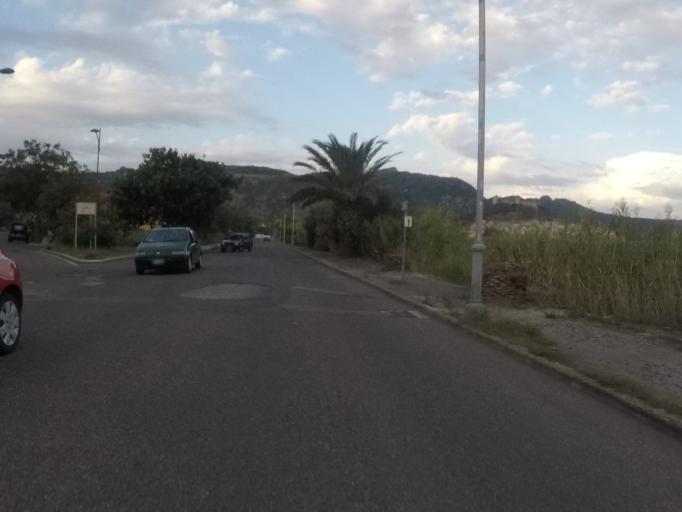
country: IT
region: Sardinia
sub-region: Provincia di Oristano
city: Bosa
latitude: 40.2930
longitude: 8.4932
